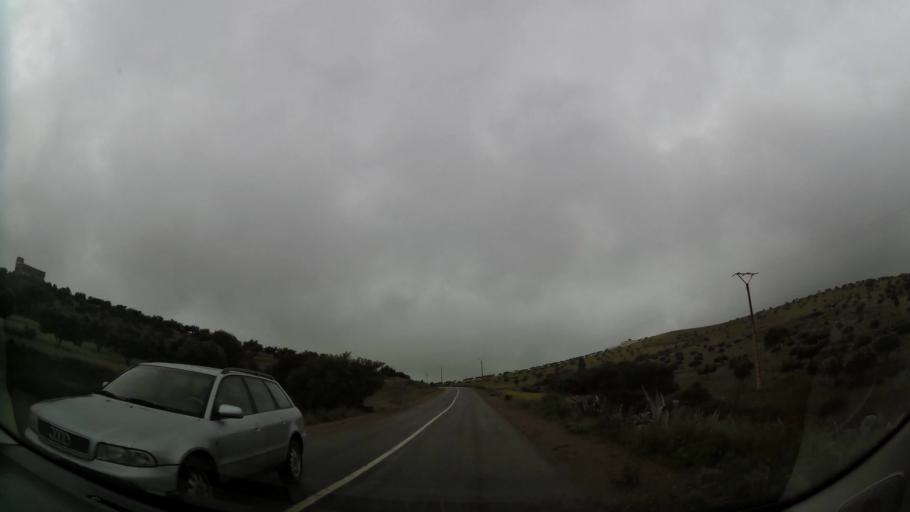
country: MA
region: Oriental
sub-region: Nador
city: Selouane
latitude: 35.1221
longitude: -3.0616
